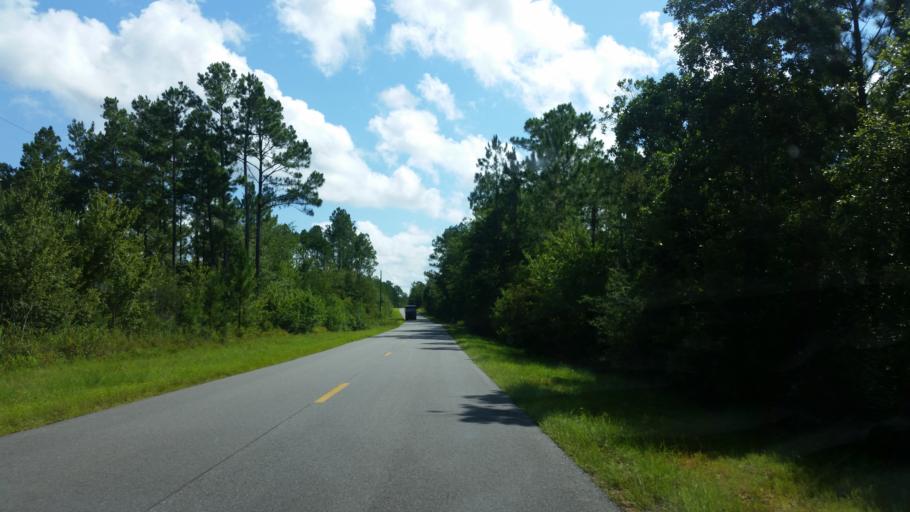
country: US
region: Florida
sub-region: Santa Rosa County
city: Point Baker
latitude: 30.7047
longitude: -86.9394
